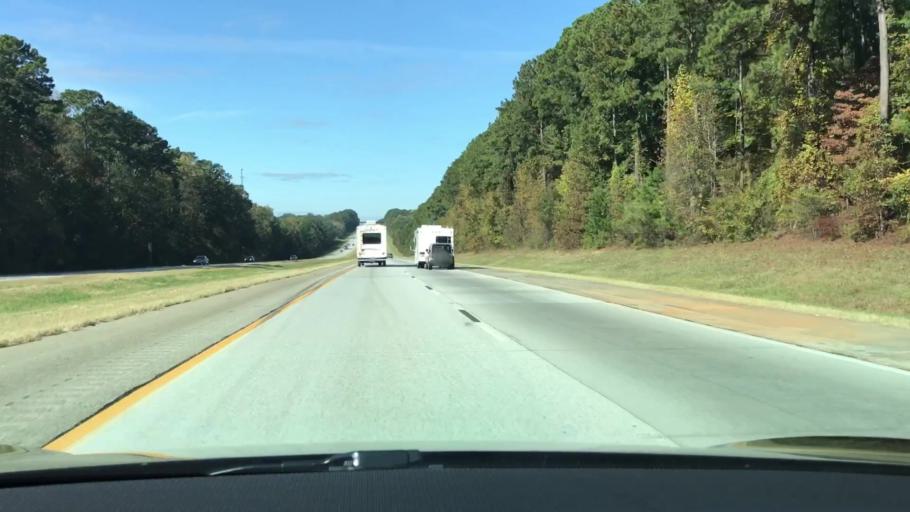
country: US
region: Georgia
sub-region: Putnam County
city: Jefferson
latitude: 33.5336
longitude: -83.2943
